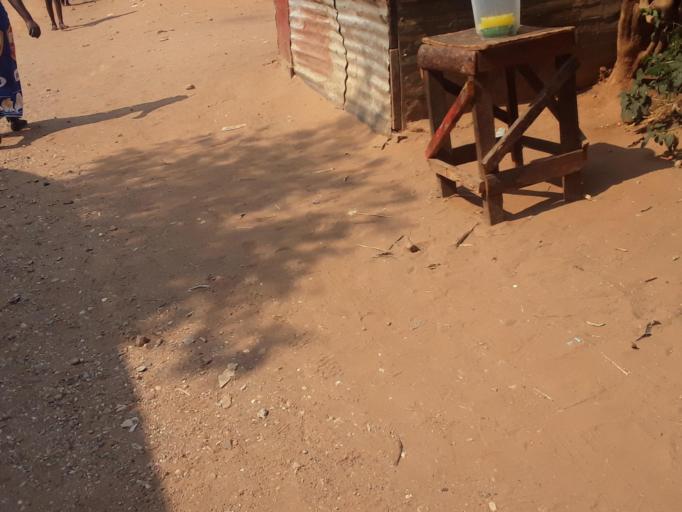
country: ZM
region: Lusaka
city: Lusaka
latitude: -15.3553
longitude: 28.2968
